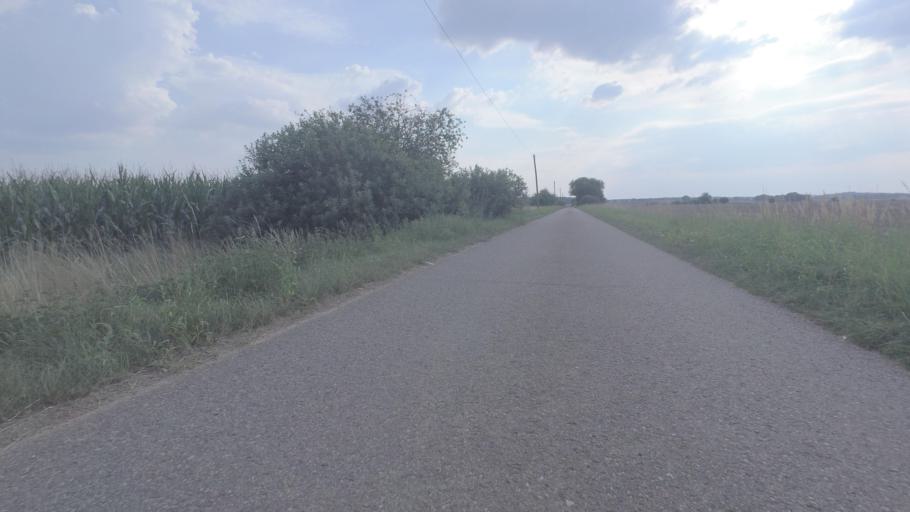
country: DE
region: Brandenburg
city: Wittstock
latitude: 53.2426
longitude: 12.4645
